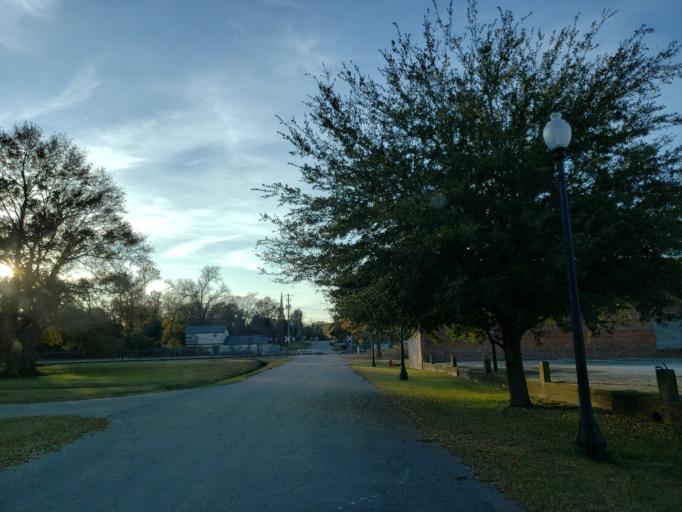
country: US
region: Mississippi
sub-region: Forrest County
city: Hattiesburg
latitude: 31.3345
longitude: -89.2933
